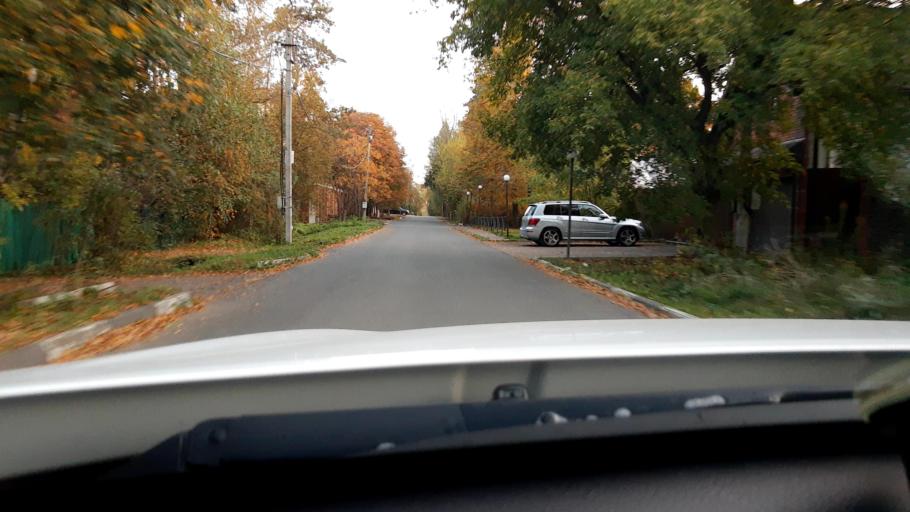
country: RU
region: Moskovskaya
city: Nemchinovka
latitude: 55.7248
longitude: 37.3693
